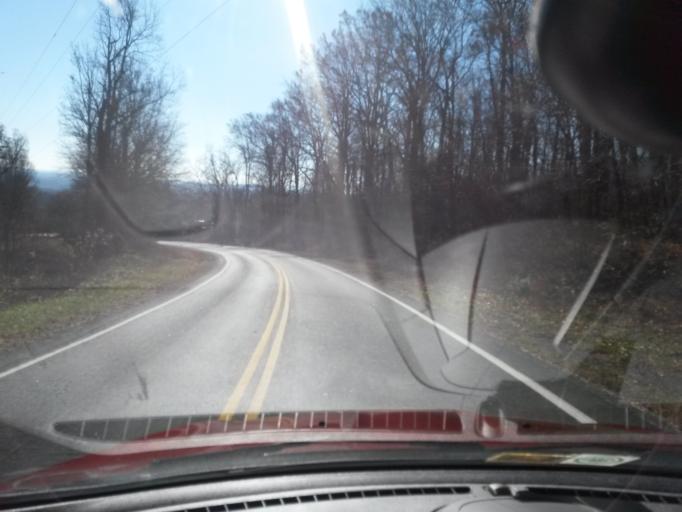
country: US
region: Virginia
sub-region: City of Bedford
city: Bedford
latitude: 37.4314
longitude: -79.5753
